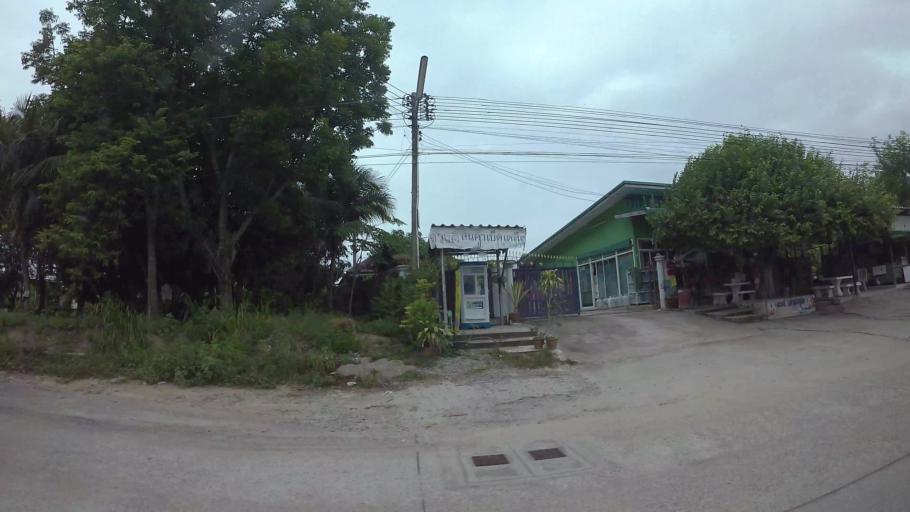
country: TH
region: Chon Buri
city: Si Racha
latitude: 13.1835
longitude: 100.9813
